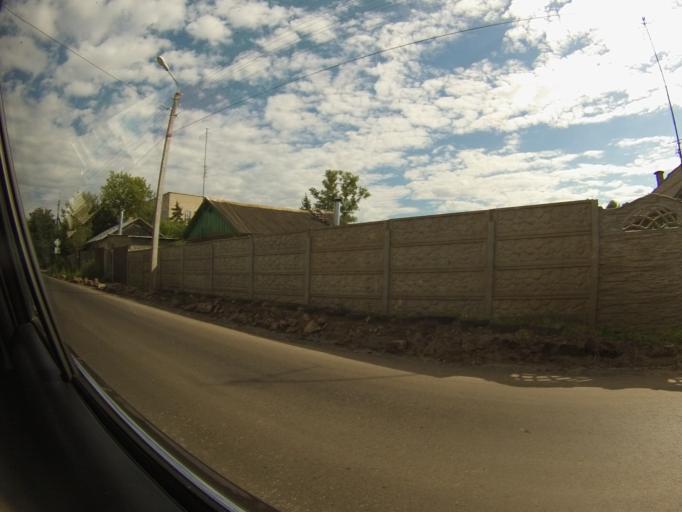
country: RU
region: Orjol
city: Mtsensk
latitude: 53.2877
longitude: 36.5846
